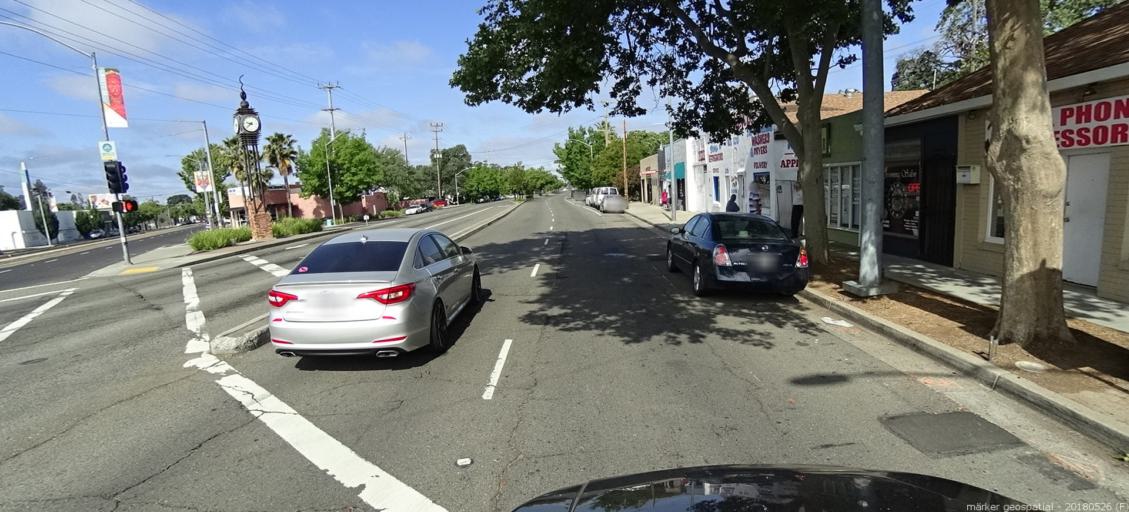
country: US
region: California
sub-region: Sacramento County
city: Sacramento
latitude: 38.6064
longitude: -121.4589
